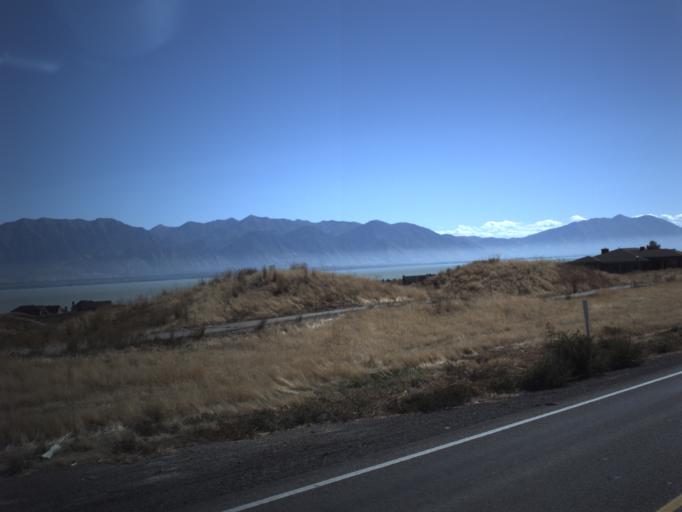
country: US
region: Utah
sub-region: Utah County
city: Saratoga Springs
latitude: 40.3244
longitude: -111.9041
